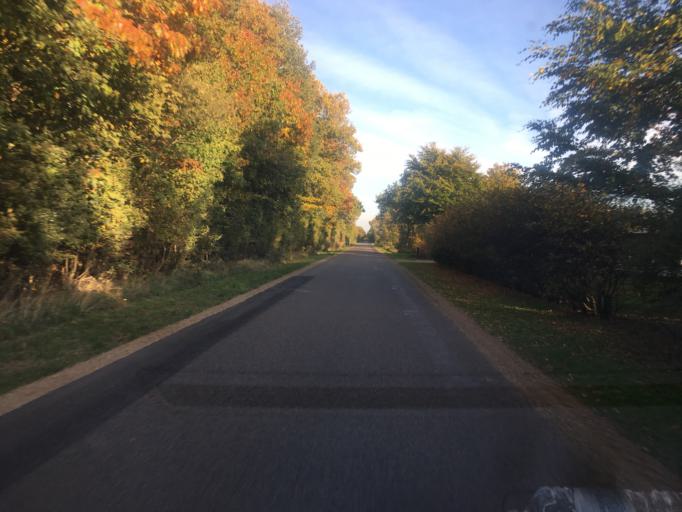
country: DE
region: Schleswig-Holstein
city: Ellhoft
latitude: 54.9150
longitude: 8.9778
